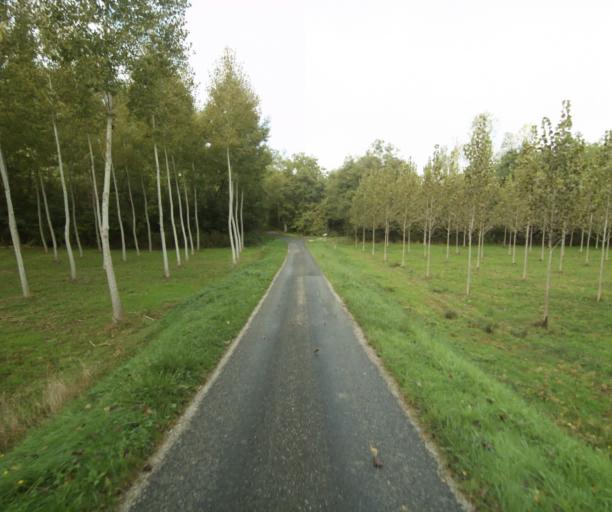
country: FR
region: Midi-Pyrenees
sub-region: Departement du Gers
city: Nogaro
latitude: 43.8344
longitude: -0.0761
